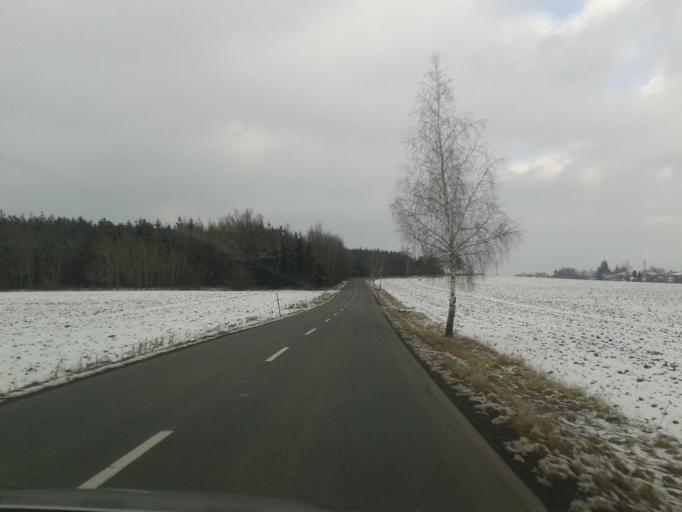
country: CZ
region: Olomoucky
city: Konice
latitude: 49.6005
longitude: 16.8896
